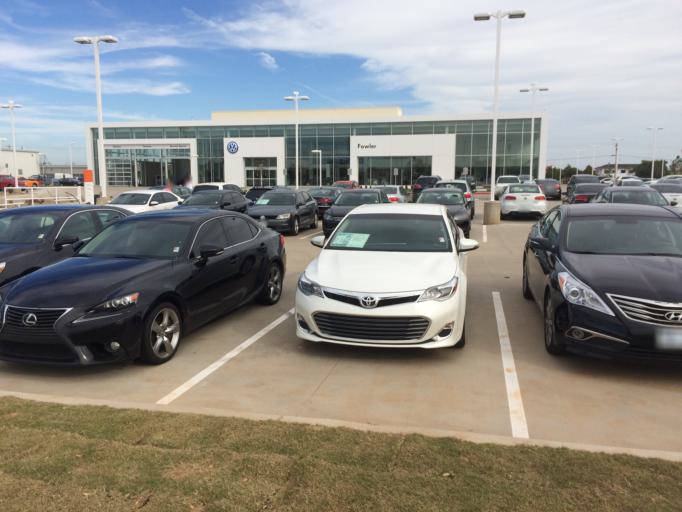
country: US
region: Oklahoma
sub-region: Cleveland County
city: Norman
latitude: 35.2267
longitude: -97.4852
